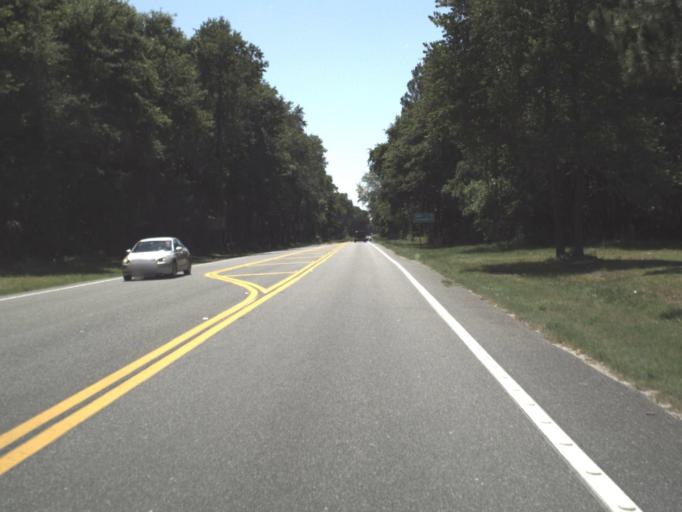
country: US
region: Florida
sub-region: Lafayette County
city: Mayo
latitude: 30.1292
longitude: -83.2938
